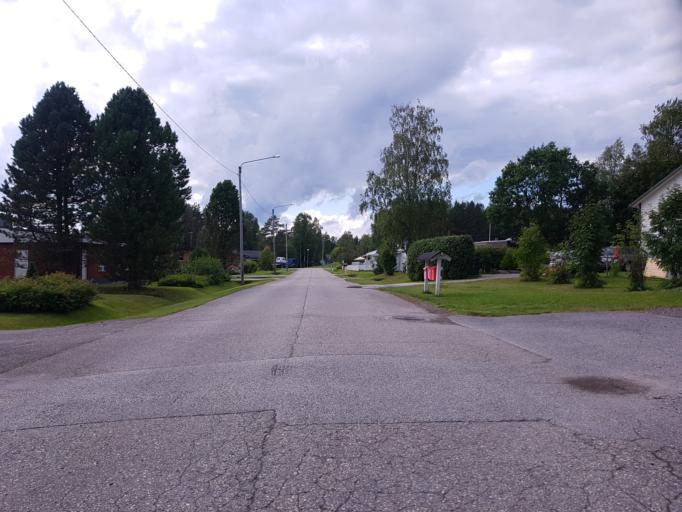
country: FI
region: Kainuu
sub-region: Kehys-Kainuu
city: Kuhmo
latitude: 64.1243
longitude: 29.5408
